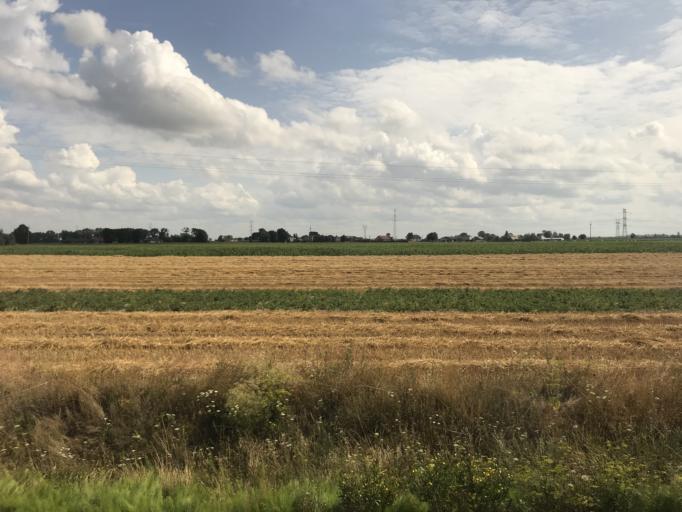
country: PL
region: Kujawsko-Pomorskie
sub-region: Powiat inowroclawski
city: Zlotniki Kujawskie
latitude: 52.8987
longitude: 18.1528
